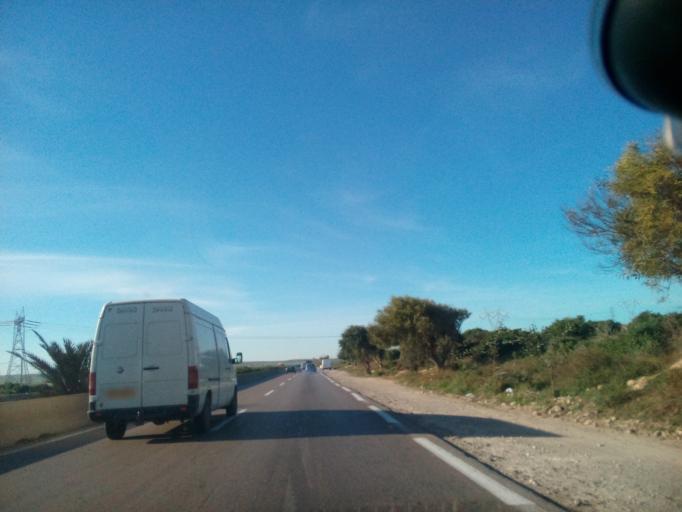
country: DZ
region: Oran
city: Ain el Bya
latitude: 35.7809
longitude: -0.1862
